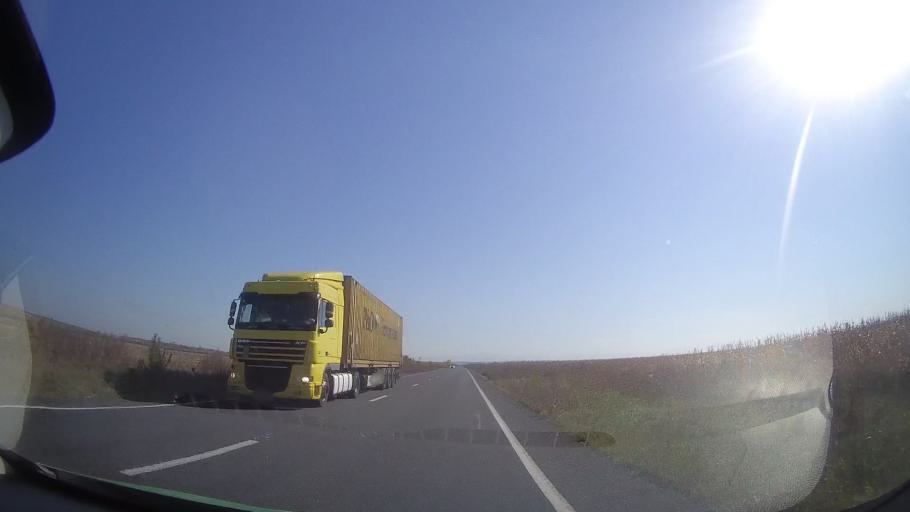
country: RO
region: Timis
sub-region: Comuna Belint
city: Belint
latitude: 45.7452
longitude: 21.8026
